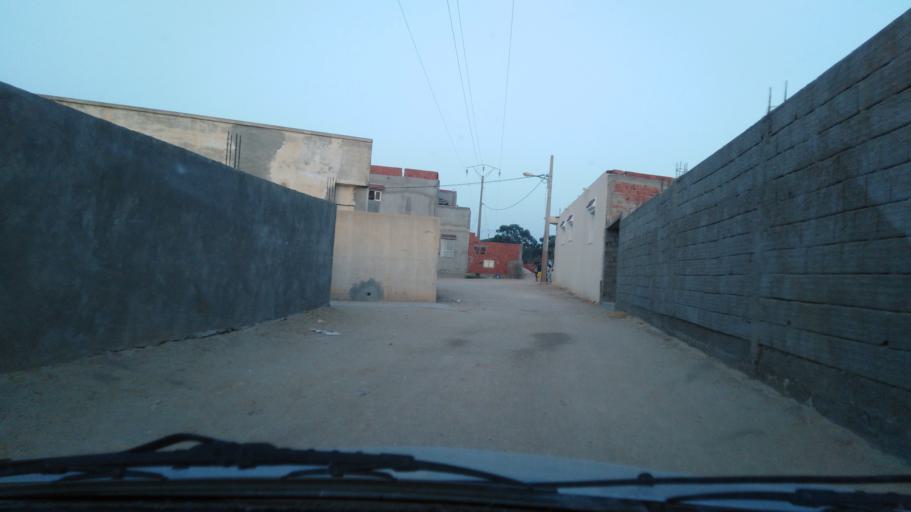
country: TN
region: Qabis
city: Gabes
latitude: 33.9531
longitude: 9.9973
